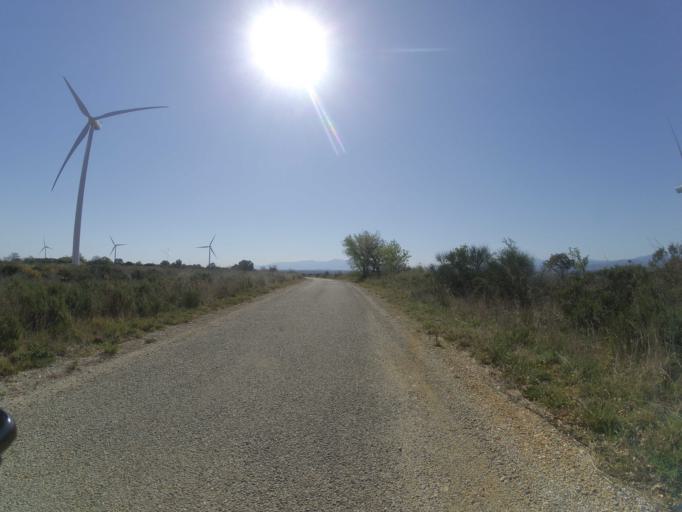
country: FR
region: Languedoc-Roussillon
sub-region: Departement des Pyrenees-Orientales
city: Pezilla-la-Riviere
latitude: 42.7176
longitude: 2.7717
